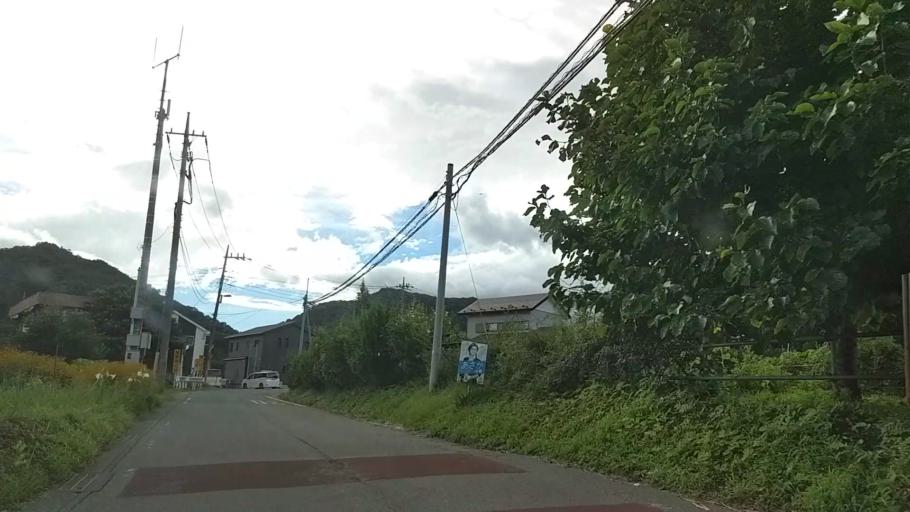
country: JP
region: Yamanashi
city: Uenohara
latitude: 35.5941
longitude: 139.1489
